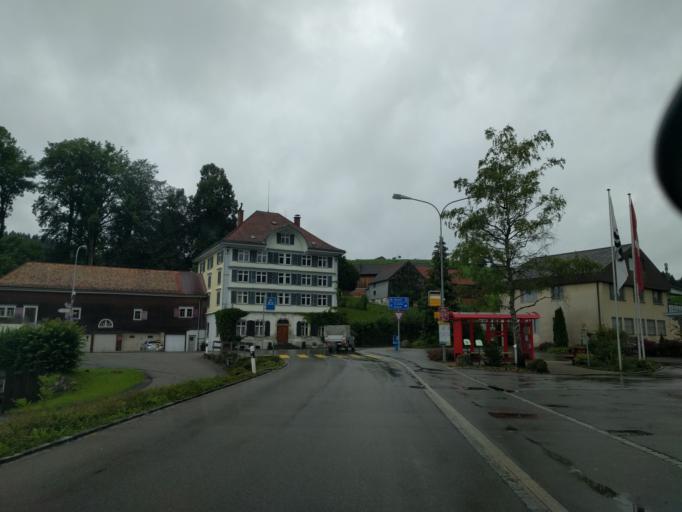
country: CH
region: Appenzell Ausserrhoden
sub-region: Bezirk Hinterland
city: Schwellbrunn
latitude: 47.3286
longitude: 9.2270
